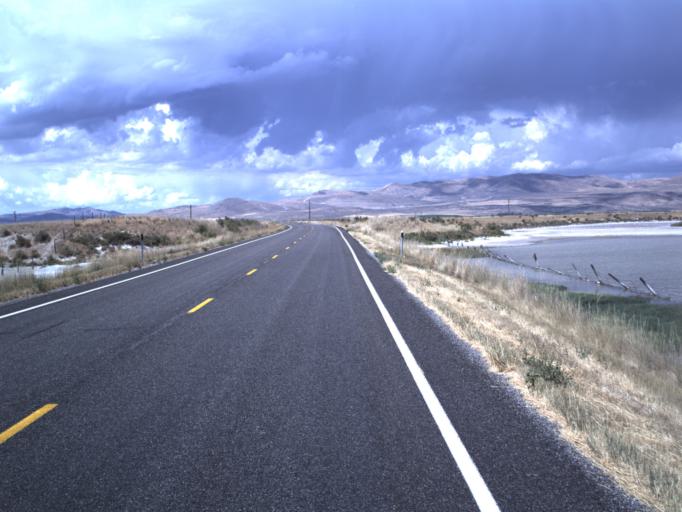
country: US
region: Utah
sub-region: Box Elder County
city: Tremonton
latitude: 41.5880
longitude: -112.2690
